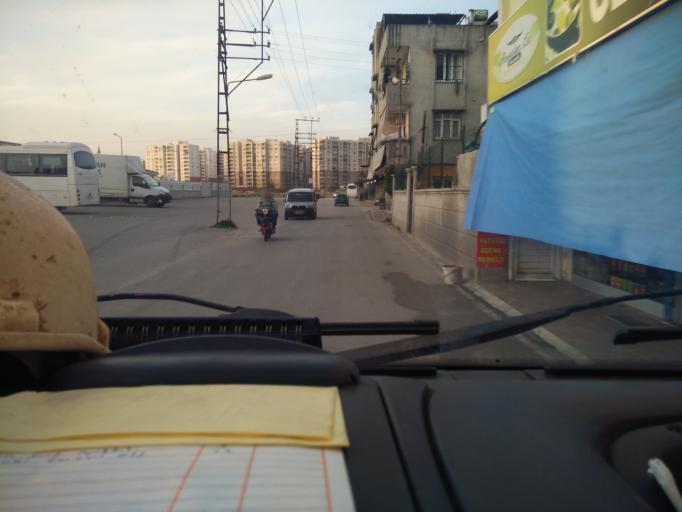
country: TR
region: Adana
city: Seyhan
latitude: 37.0040
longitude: 35.2799
